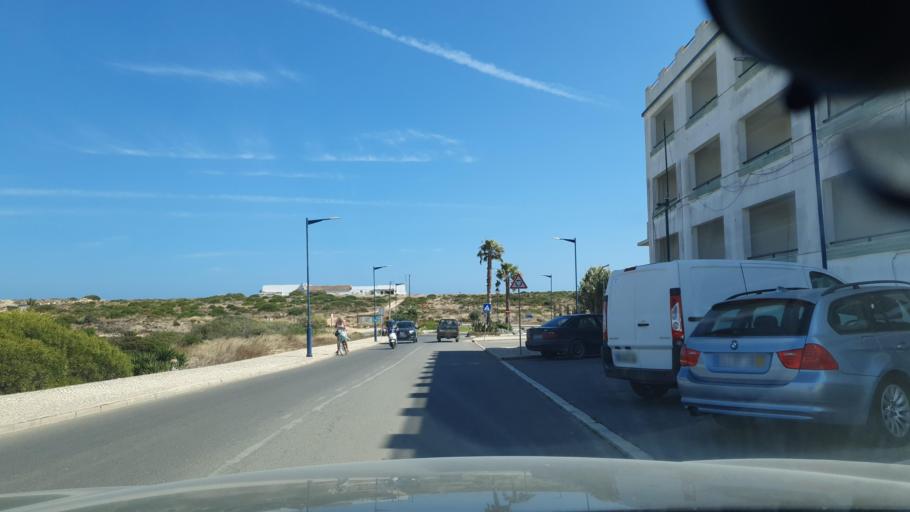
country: PT
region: Faro
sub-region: Vila do Bispo
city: Sagres
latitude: 37.0095
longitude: -8.9318
